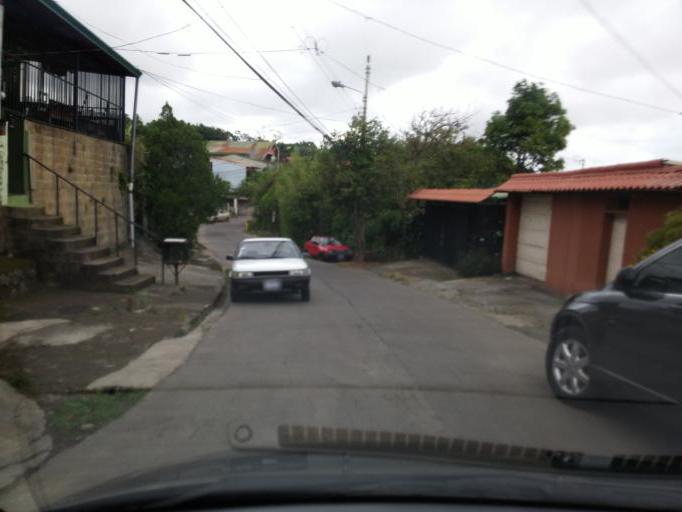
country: CR
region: Heredia
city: Mercedes
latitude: 10.0302
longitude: -84.1342
